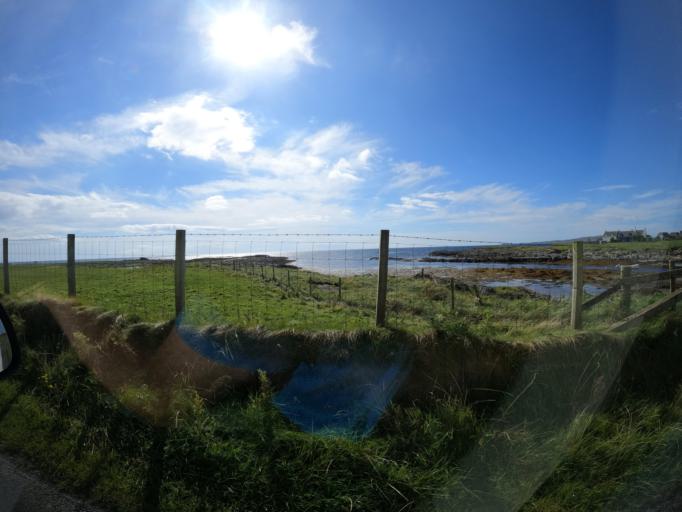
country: GB
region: Scotland
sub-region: Eilean Siar
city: Barra
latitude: 56.4918
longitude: -6.8317
